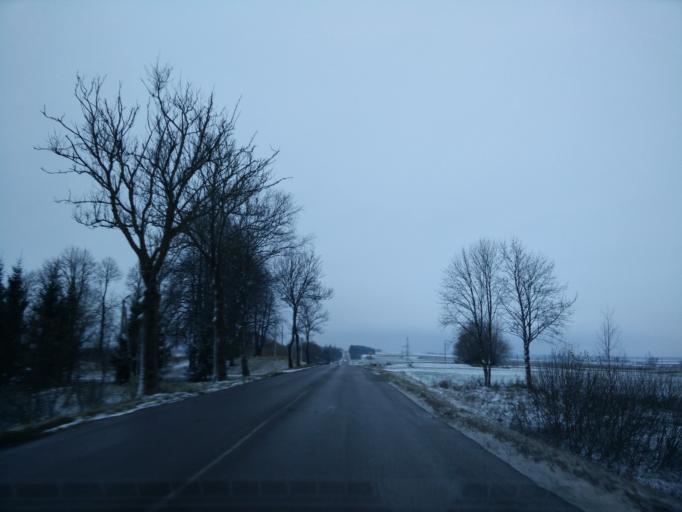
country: LT
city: Kelme
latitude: 55.6176
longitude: 22.9093
